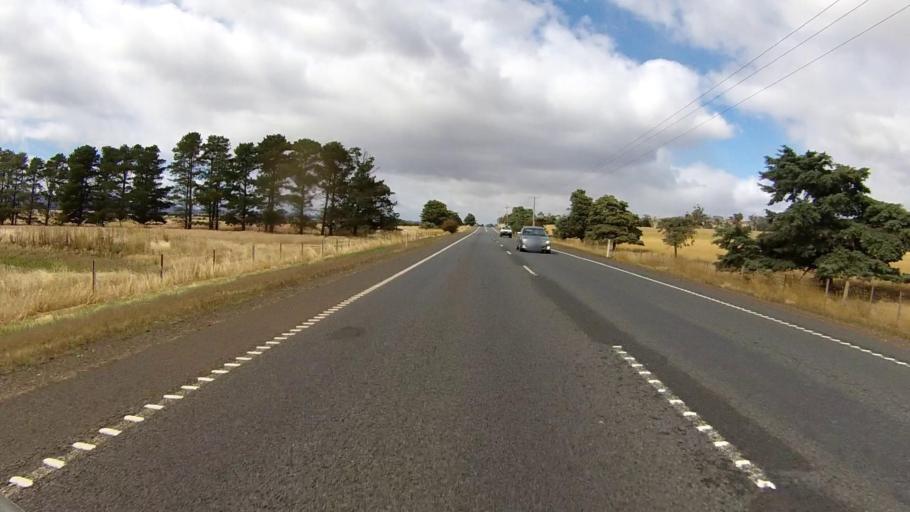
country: AU
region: Tasmania
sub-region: Northern Midlands
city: Evandale
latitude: -41.9502
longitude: 147.4946
